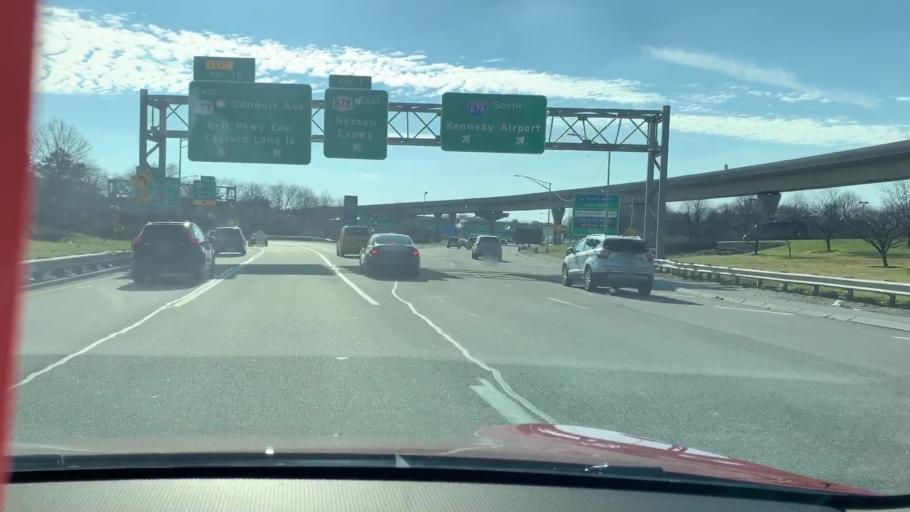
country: US
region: New York
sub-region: Queens County
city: Jamaica
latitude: 40.6656
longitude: -73.8025
